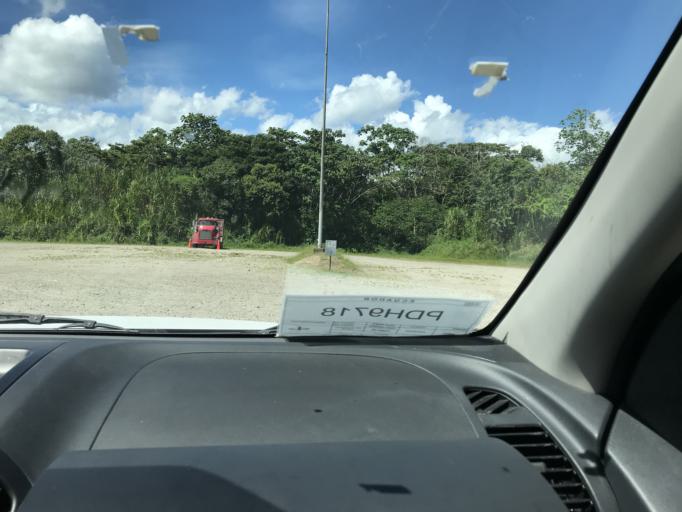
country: EC
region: Orellana
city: Puerto Francisco de Orellana
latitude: -0.4448
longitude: -76.6083
